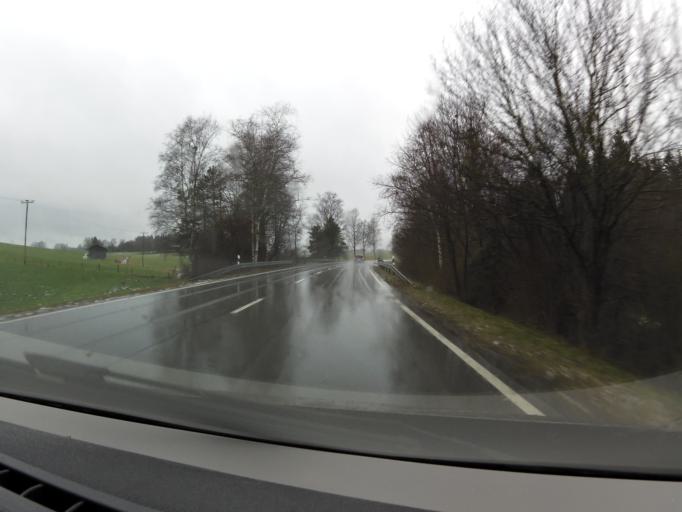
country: DE
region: Bavaria
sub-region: Upper Bavaria
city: Greiling
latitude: 47.7595
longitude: 11.6060
